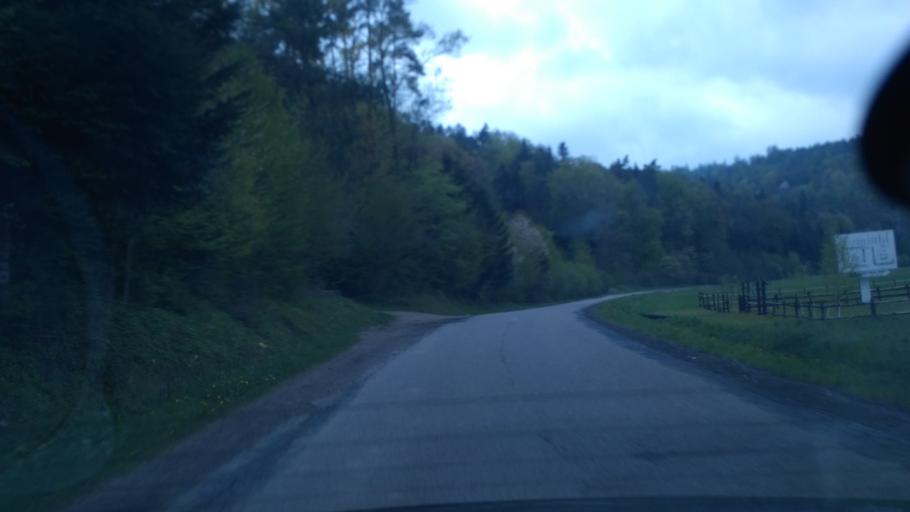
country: PL
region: Subcarpathian Voivodeship
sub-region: Powiat brzozowski
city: Nozdrzec
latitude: 49.7329
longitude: 22.2050
